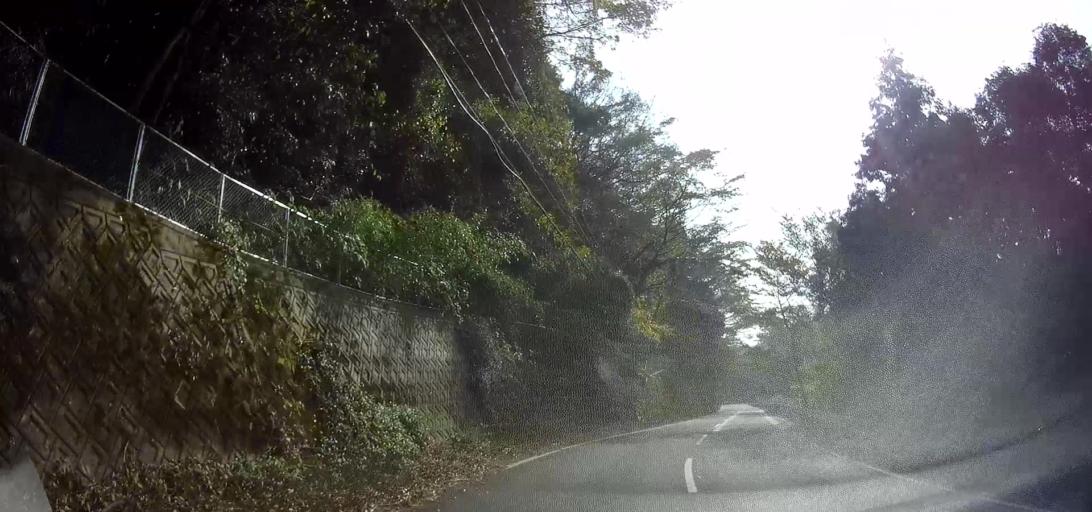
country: JP
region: Nagasaki
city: Shimabara
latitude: 32.6773
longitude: 130.2060
